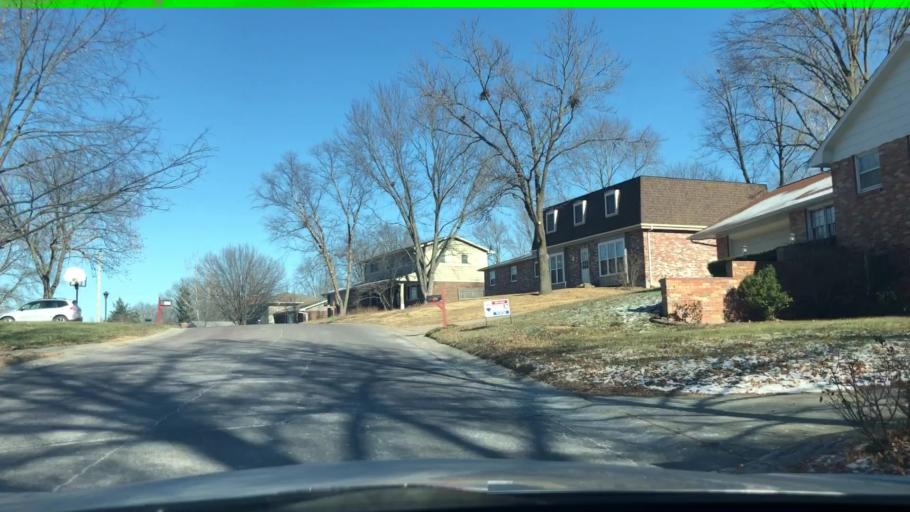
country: US
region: Missouri
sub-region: Boone County
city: Columbia
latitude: 38.9522
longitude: -92.3944
